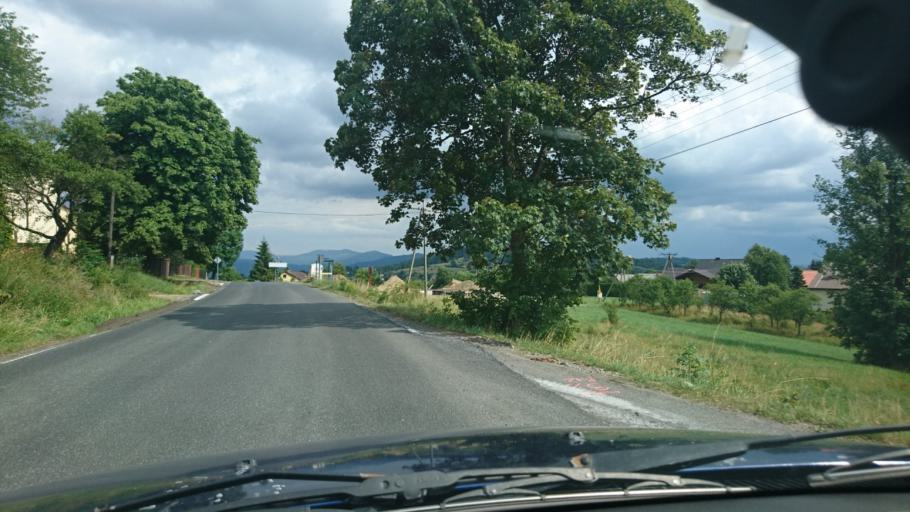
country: PL
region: Silesian Voivodeship
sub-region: Powiat zywiecki
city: Laliki
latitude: 49.5483
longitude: 19.0127
